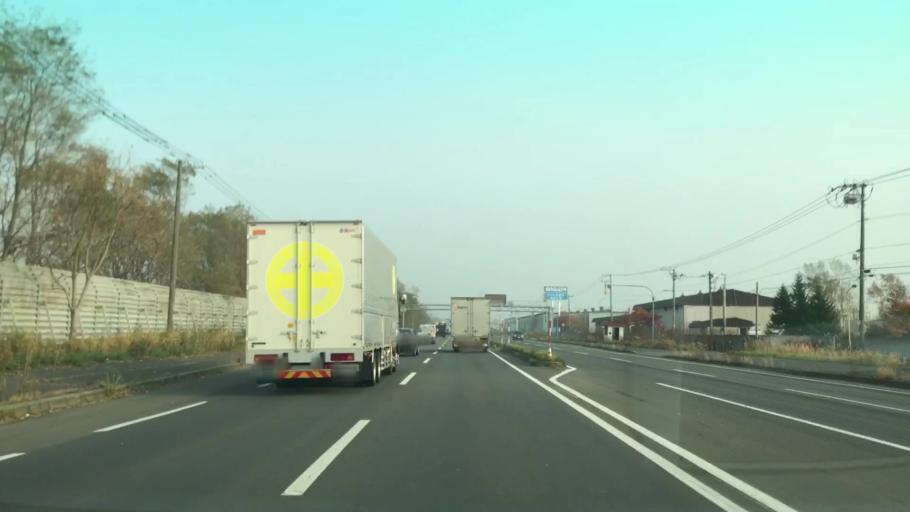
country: JP
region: Hokkaido
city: Ishikari
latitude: 43.1891
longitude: 141.3255
